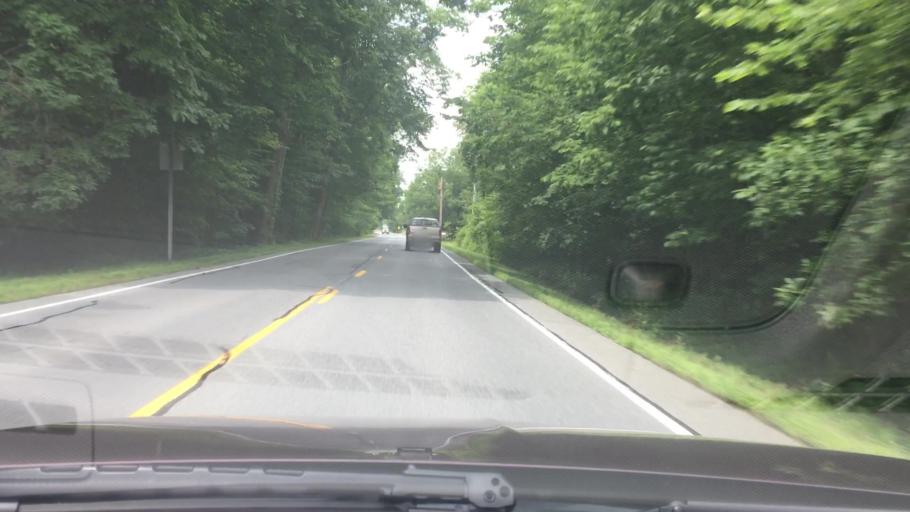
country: US
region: New York
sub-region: Dutchess County
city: Hillside Lake
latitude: 41.6454
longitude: -73.7781
